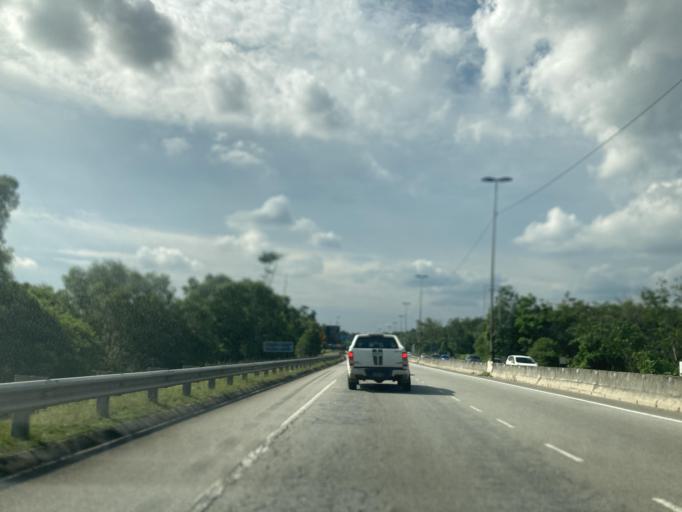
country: MY
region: Selangor
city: Kampung Baru Subang
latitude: 3.1378
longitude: 101.5526
